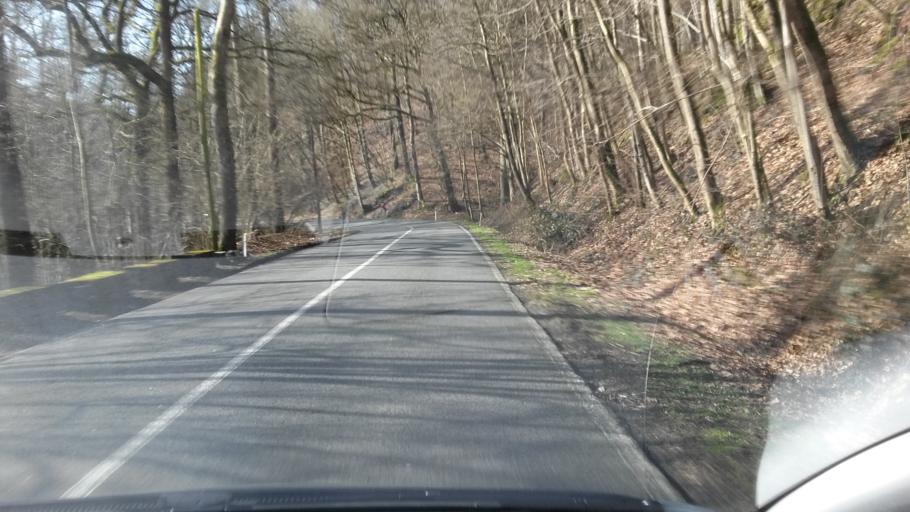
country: BE
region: Wallonia
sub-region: Province de Liege
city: Ferrieres
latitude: 50.4072
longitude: 5.6028
